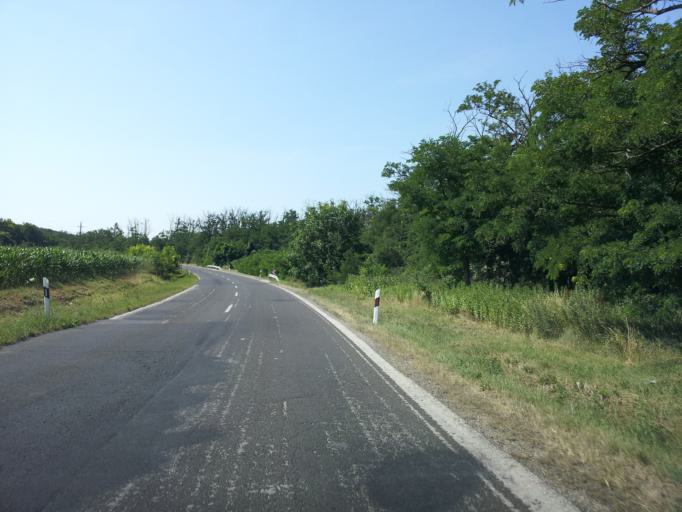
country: HU
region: Fejer
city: Lovasbereny
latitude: 47.2771
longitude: 18.5253
